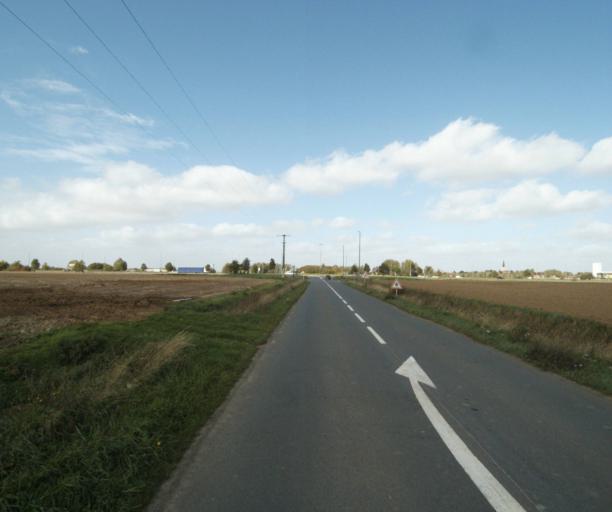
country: FR
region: Nord-Pas-de-Calais
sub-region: Departement du Nord
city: Herlies
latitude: 50.5676
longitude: 2.8570
